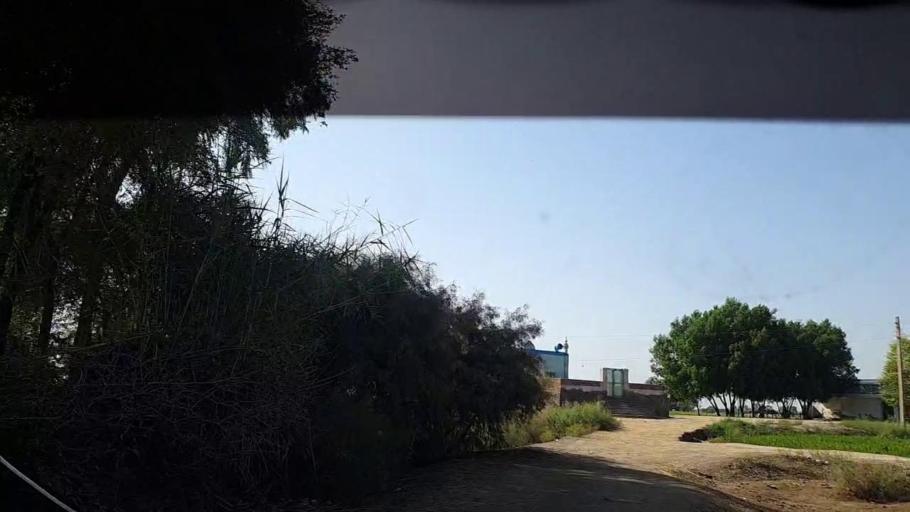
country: PK
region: Sindh
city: Ghauspur
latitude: 28.1803
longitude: 69.0269
